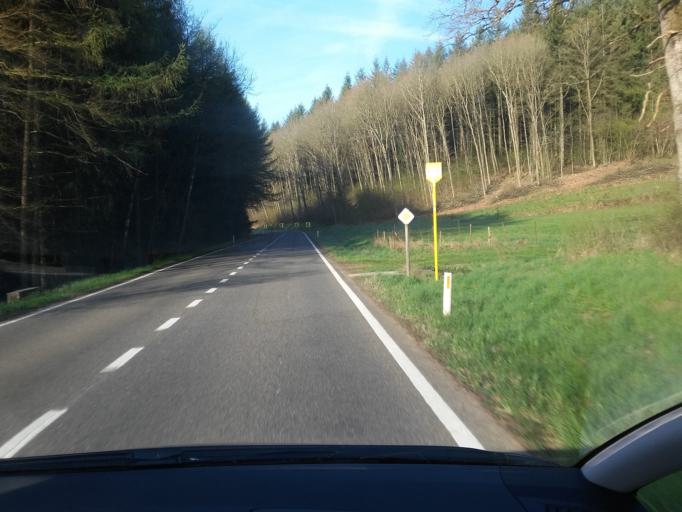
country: BE
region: Wallonia
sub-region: Province du Luxembourg
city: Saint-Leger
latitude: 49.5935
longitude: 5.6397
